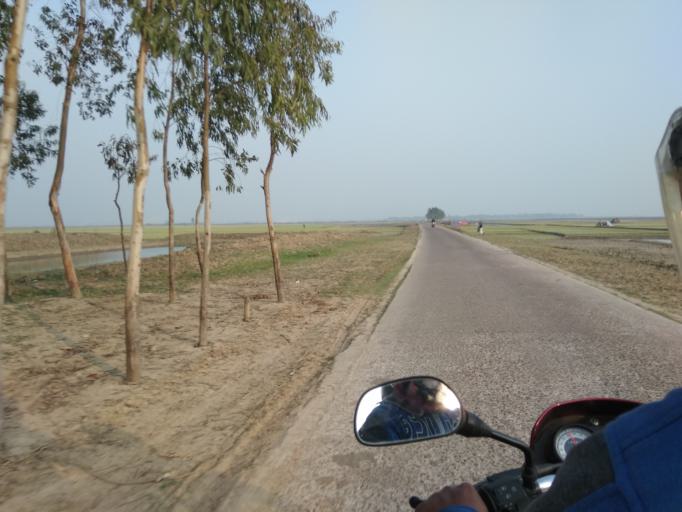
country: BD
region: Rajshahi
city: Ishurdi
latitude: 24.4861
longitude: 89.2133
